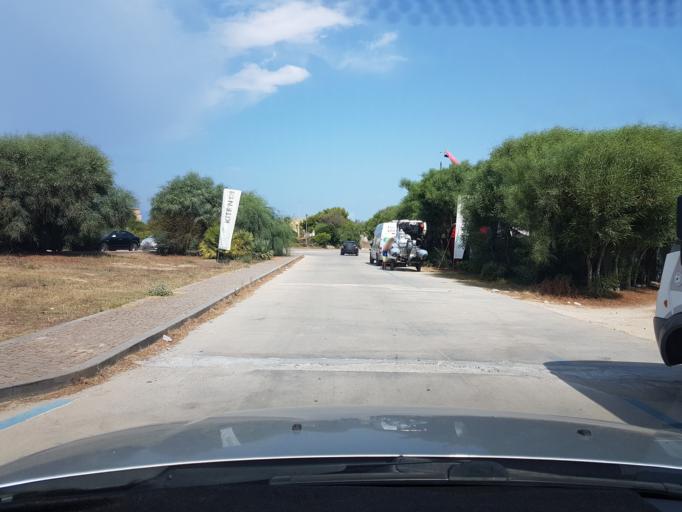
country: IT
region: Sardinia
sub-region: Provincia di Oristano
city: Cabras
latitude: 39.8839
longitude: 8.4384
